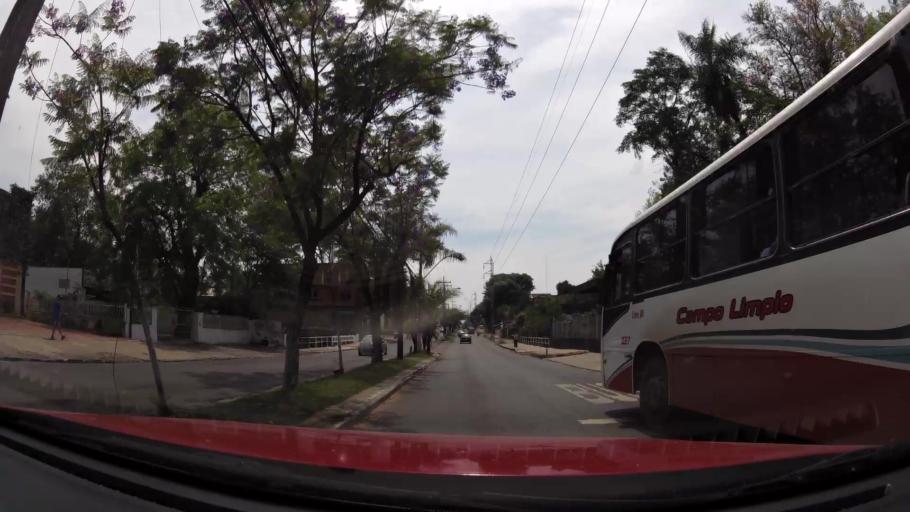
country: PY
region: Asuncion
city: Asuncion
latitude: -25.2628
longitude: -57.5926
